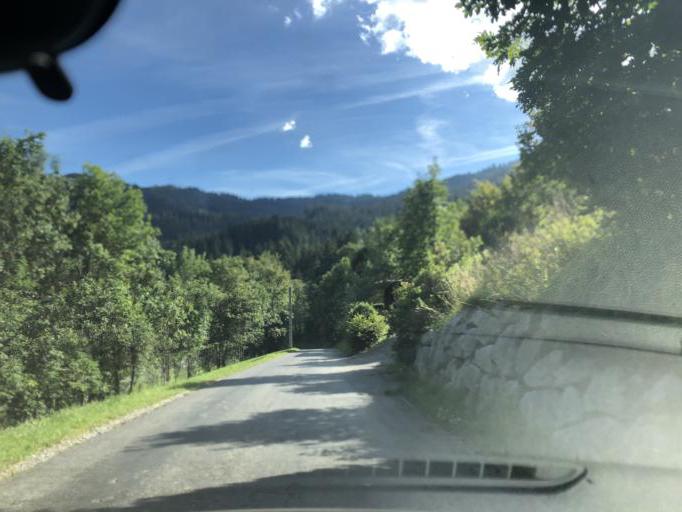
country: FR
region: Rhone-Alpes
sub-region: Departement de la Haute-Savoie
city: Cordon
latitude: 45.9078
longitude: 6.5882
